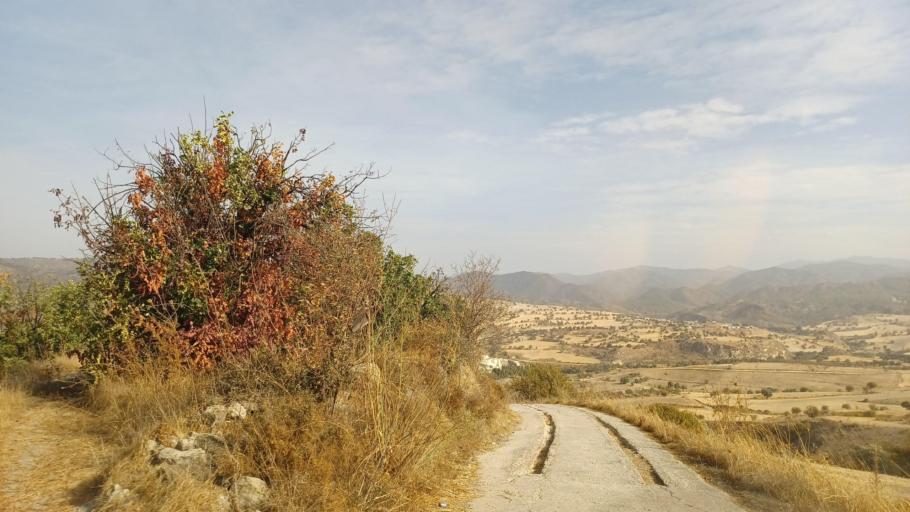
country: CY
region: Pafos
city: Polis
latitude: 34.9447
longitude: 32.5157
